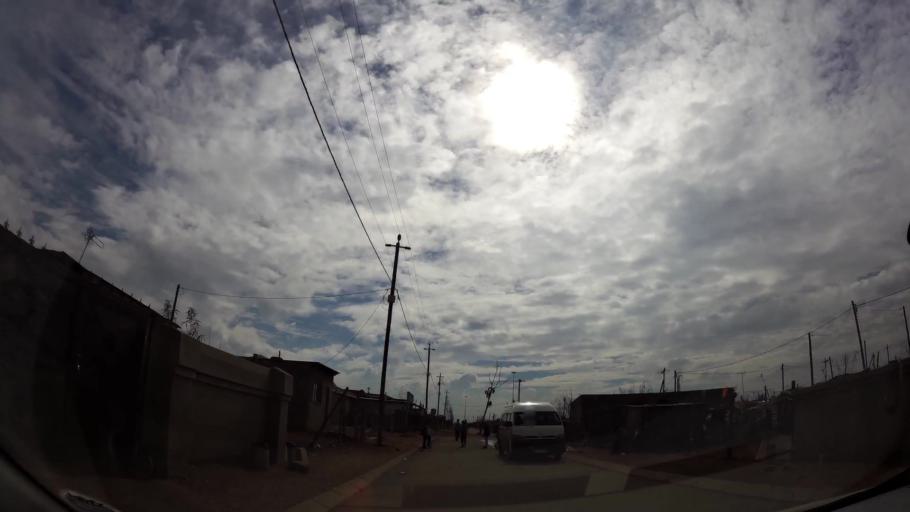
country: ZA
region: Gauteng
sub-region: Ekurhuleni Metropolitan Municipality
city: Germiston
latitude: -26.3758
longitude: 28.1687
